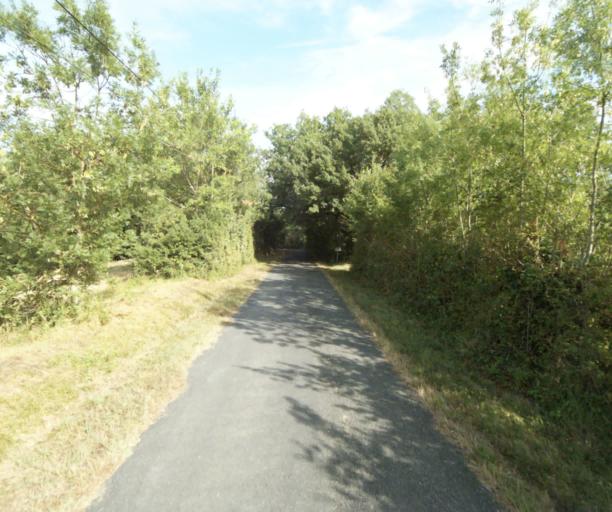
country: FR
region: Midi-Pyrenees
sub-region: Departement du Tarn
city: Soual
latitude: 43.5294
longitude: 2.0705
